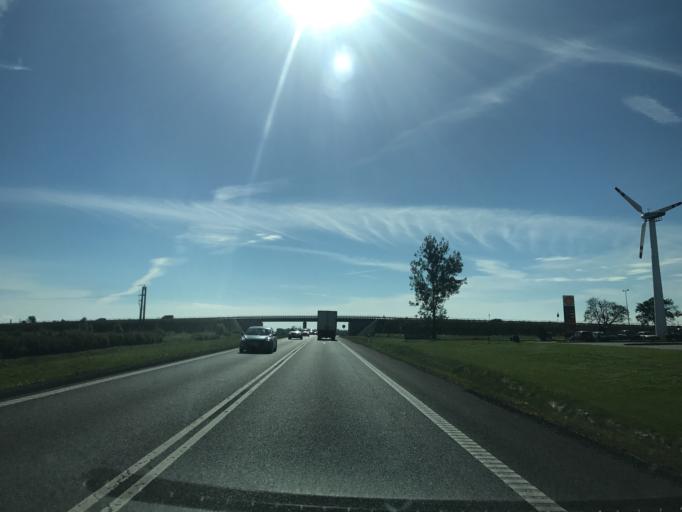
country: PL
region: Pomeranian Voivodeship
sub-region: Powiat chojnicki
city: Chojnice
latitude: 53.6819
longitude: 17.5382
